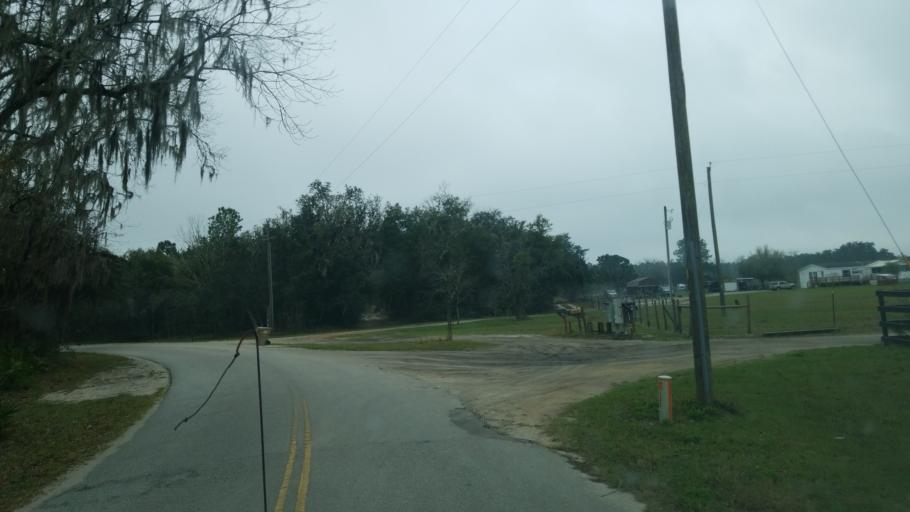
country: US
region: Florida
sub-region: Lake County
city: Groveland
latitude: 28.3839
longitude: -81.8503
